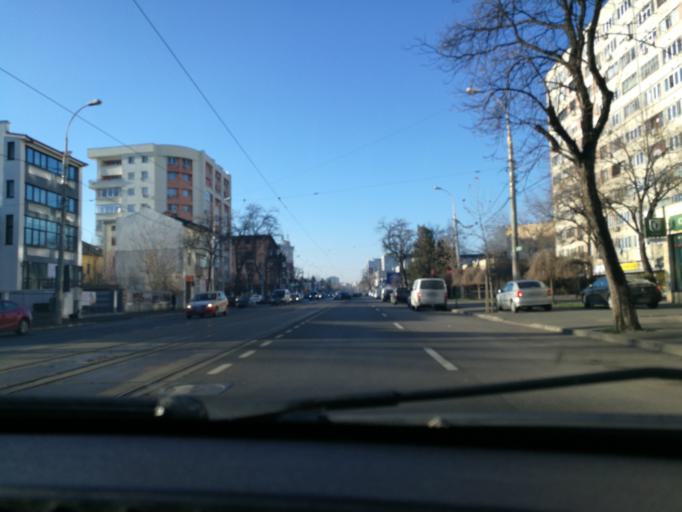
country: RO
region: Bucuresti
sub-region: Municipiul Bucuresti
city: Bucuresti
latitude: 44.4646
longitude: 26.0694
